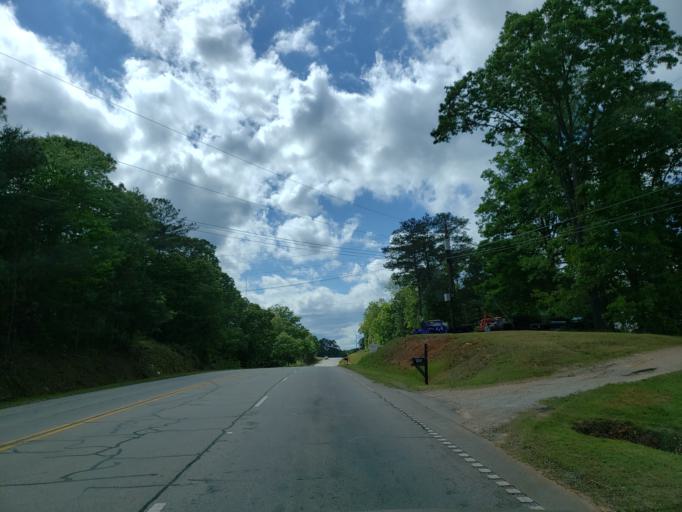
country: US
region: Georgia
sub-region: Haralson County
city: Tallapoosa
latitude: 33.7339
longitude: -85.2463
